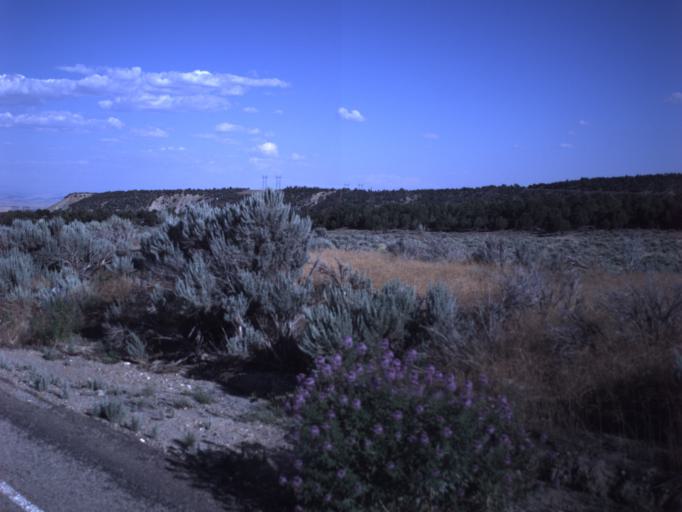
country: US
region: Utah
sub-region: Emery County
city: Huntington
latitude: 39.4842
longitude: -110.9975
